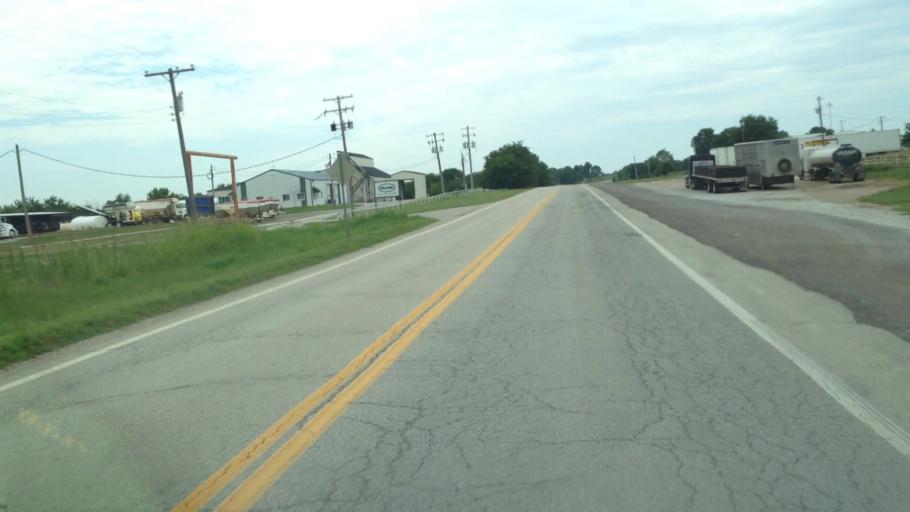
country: US
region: Kansas
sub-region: Labette County
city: Chetopa
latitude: 36.8788
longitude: -95.0989
